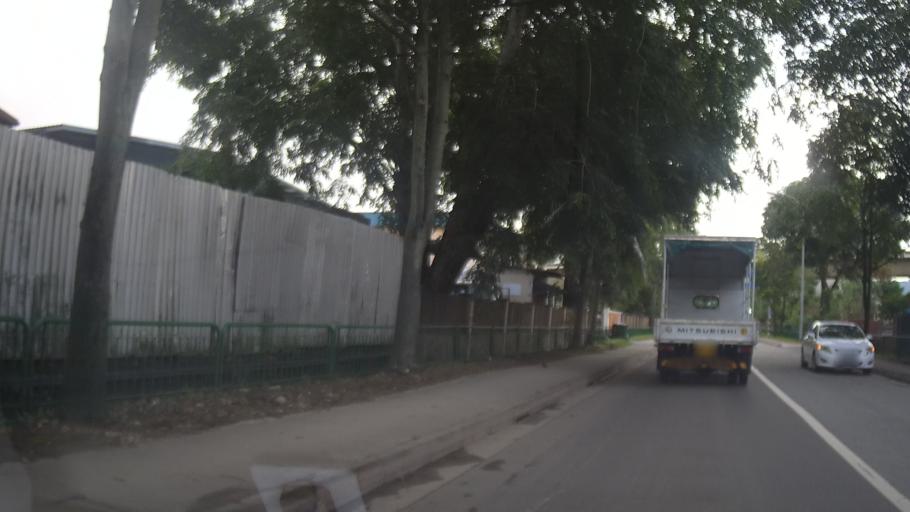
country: MY
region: Johor
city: Johor Bahru
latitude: 1.4191
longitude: 103.7476
